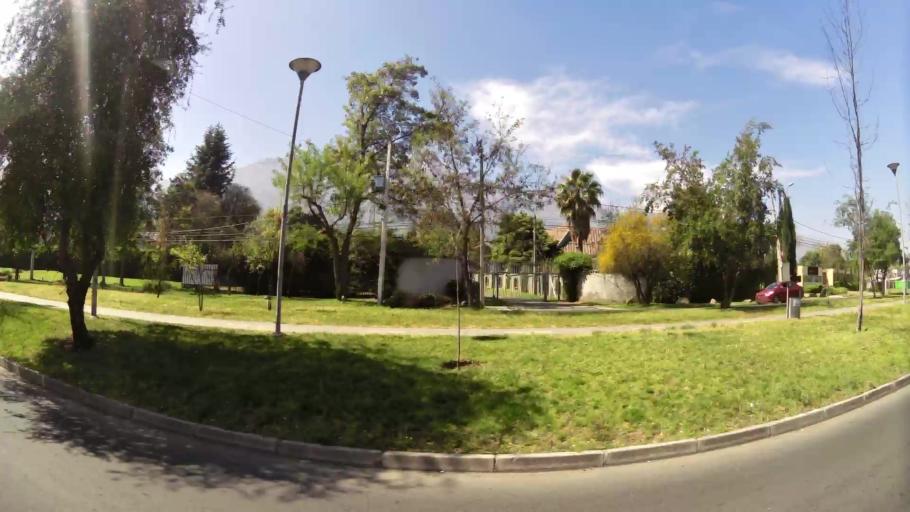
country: CL
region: Santiago Metropolitan
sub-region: Provincia de Santiago
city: Villa Presidente Frei, Nunoa, Santiago, Chile
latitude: -33.4546
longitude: -70.5293
